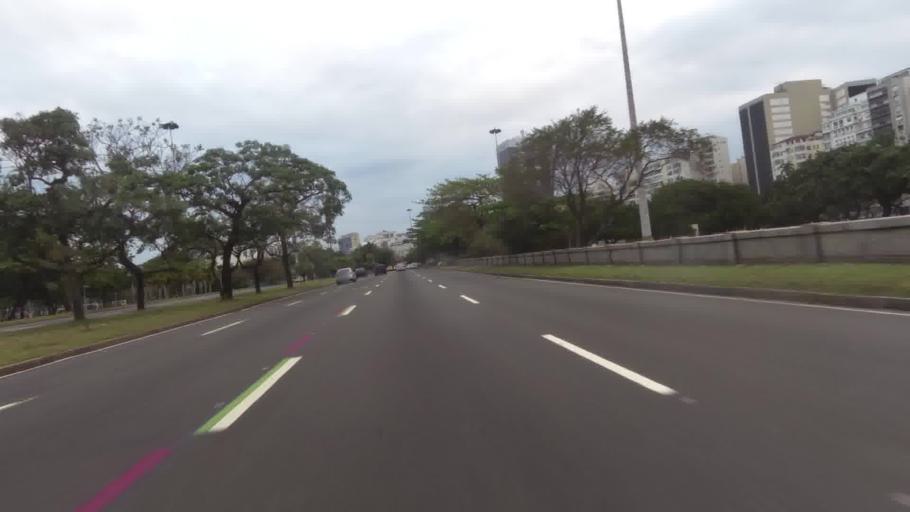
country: BR
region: Rio de Janeiro
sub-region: Rio De Janeiro
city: Rio de Janeiro
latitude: -22.9287
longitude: -43.1727
